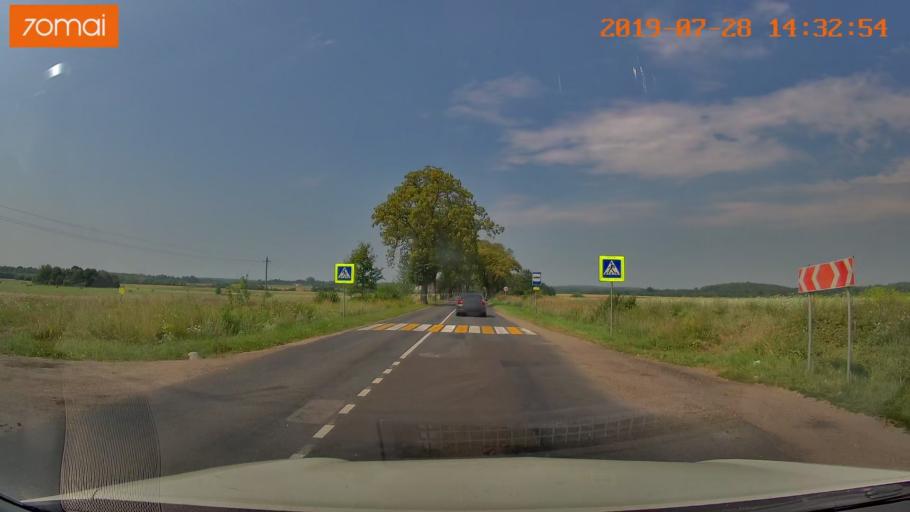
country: RU
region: Kaliningrad
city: Primorsk
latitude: 54.8157
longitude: 20.0370
